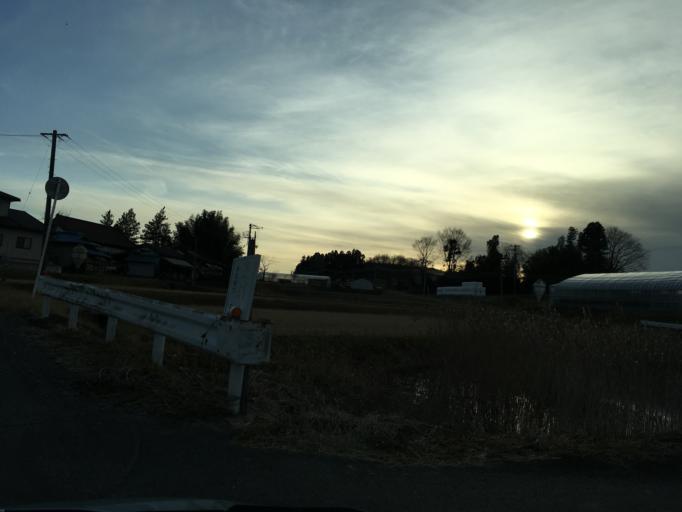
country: JP
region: Miyagi
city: Kogota
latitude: 38.6835
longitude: 141.0959
